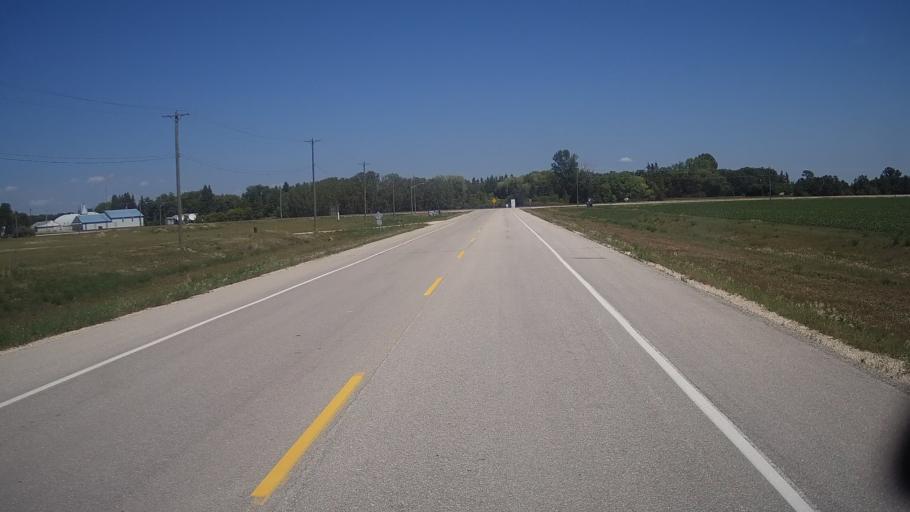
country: CA
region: Manitoba
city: Stonewall
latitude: 50.1271
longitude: -97.5433
